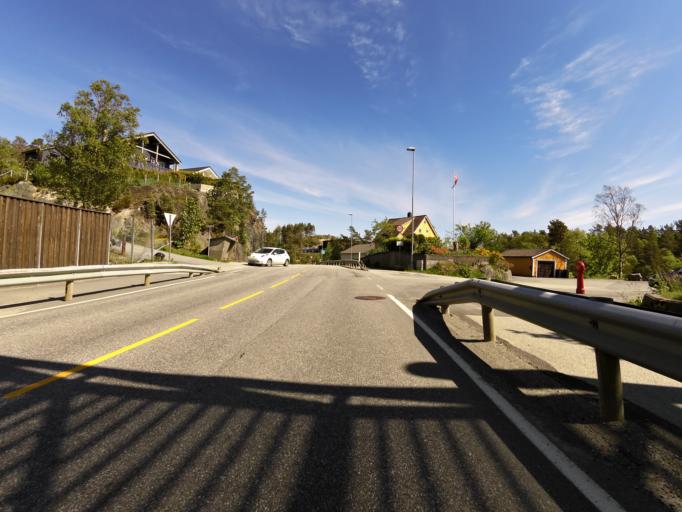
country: NO
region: Hordaland
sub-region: Stord
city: Sagvag
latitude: 59.7797
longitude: 5.3920
